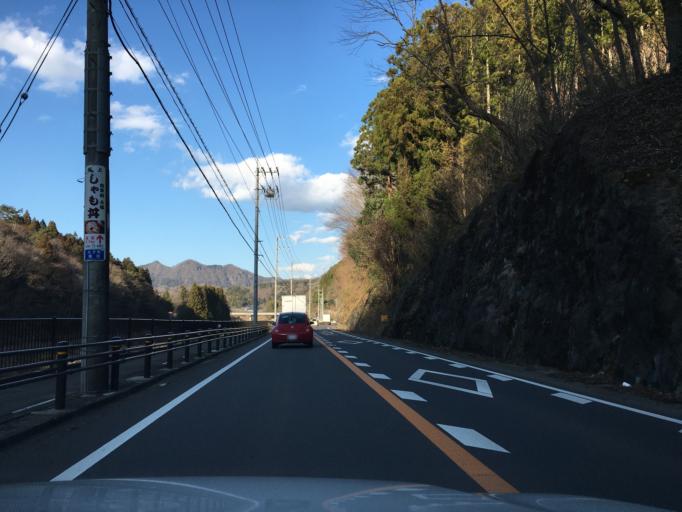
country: JP
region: Ibaraki
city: Daigo
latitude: 36.7389
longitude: 140.3776
